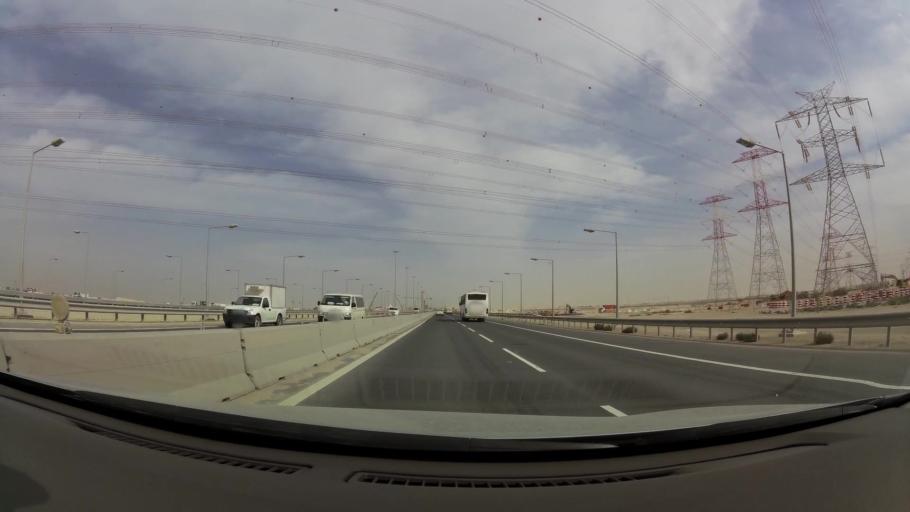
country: QA
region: Baladiyat ar Rayyan
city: Ash Shahaniyah
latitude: 25.3424
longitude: 51.3139
